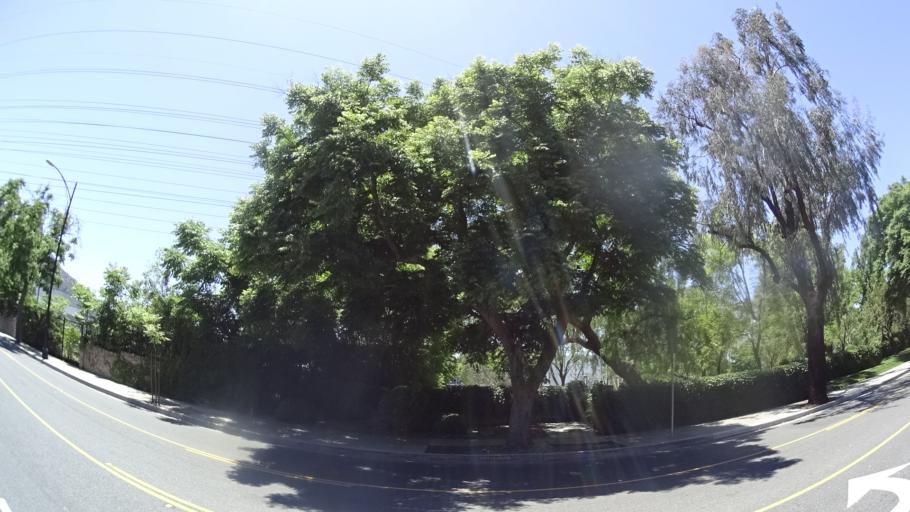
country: US
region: California
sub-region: Los Angeles County
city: Universal City
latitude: 34.1561
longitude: -118.3319
